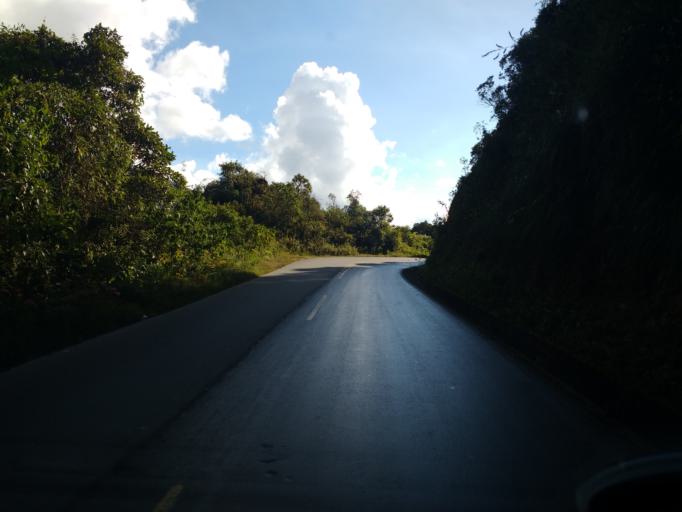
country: PE
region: Cusco
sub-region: Provincia de La Convencion
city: Santa Teresa
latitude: -13.0688
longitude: -72.3935
